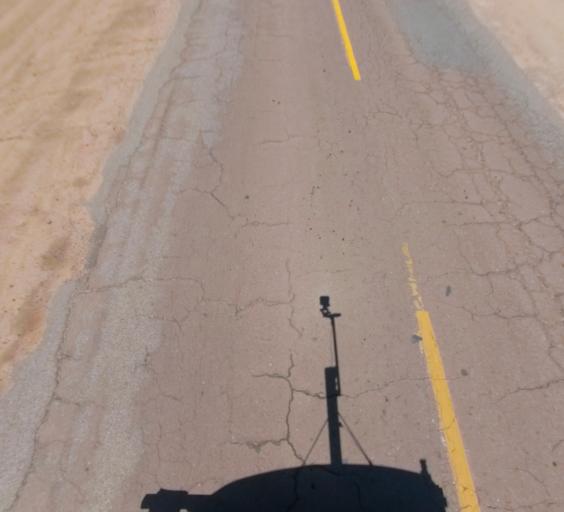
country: US
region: California
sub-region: Madera County
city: Bonadelle Ranchos-Madera Ranchos
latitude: 36.8946
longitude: -119.8237
